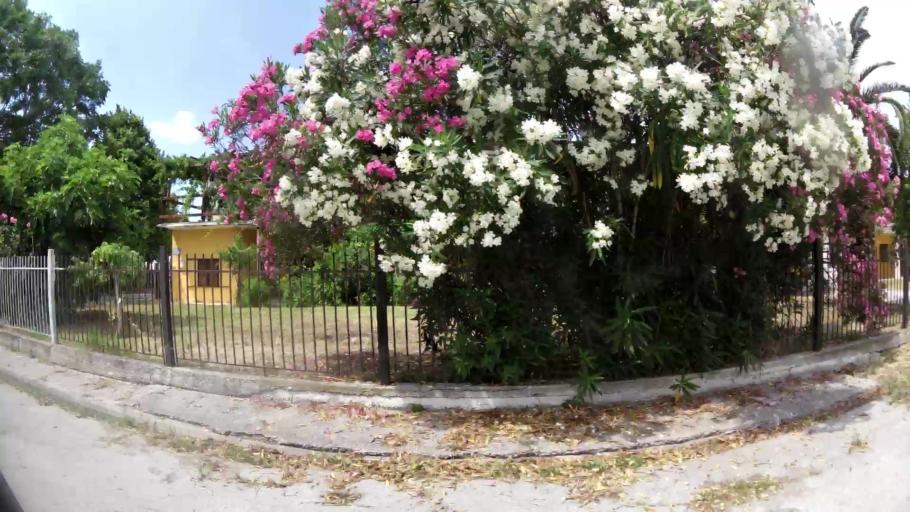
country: GR
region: Central Macedonia
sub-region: Nomos Pierias
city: Korinos
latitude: 40.3123
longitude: 22.5942
